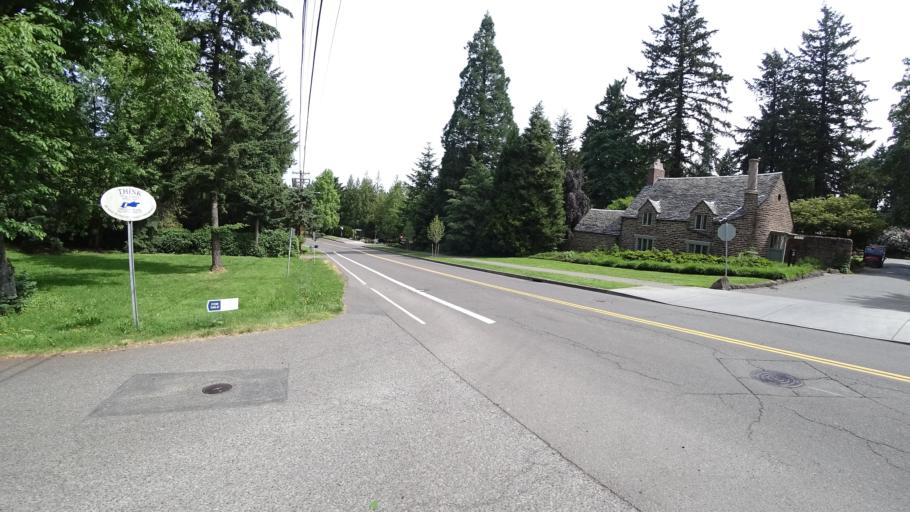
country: US
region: Oregon
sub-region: Clackamas County
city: Lake Oswego
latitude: 45.4503
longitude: -122.6727
